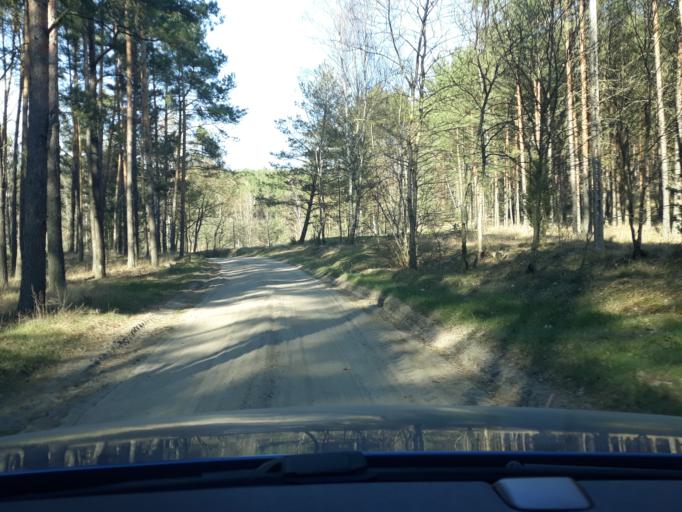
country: PL
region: Pomeranian Voivodeship
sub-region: Powiat bytowski
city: Lipnica
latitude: 53.9110
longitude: 17.4311
